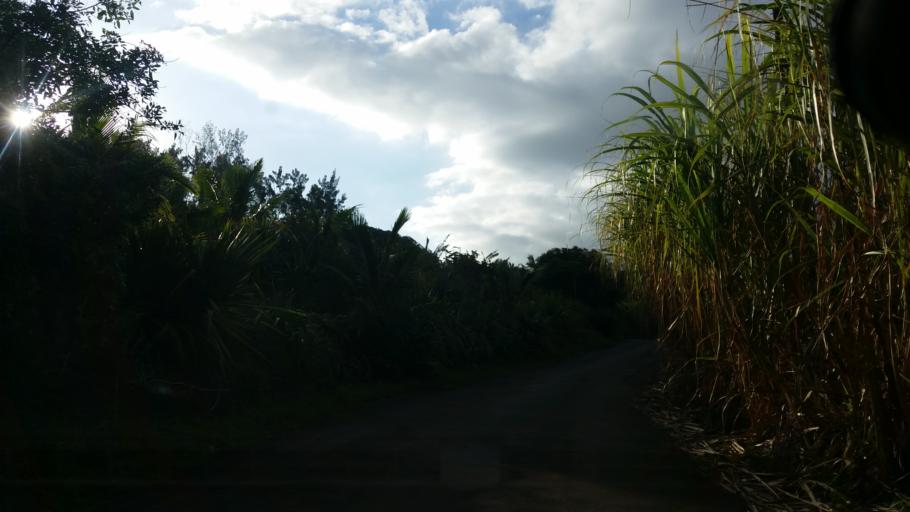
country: RE
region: Reunion
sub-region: Reunion
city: Saint-Joseph
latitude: -21.3799
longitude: 55.6707
